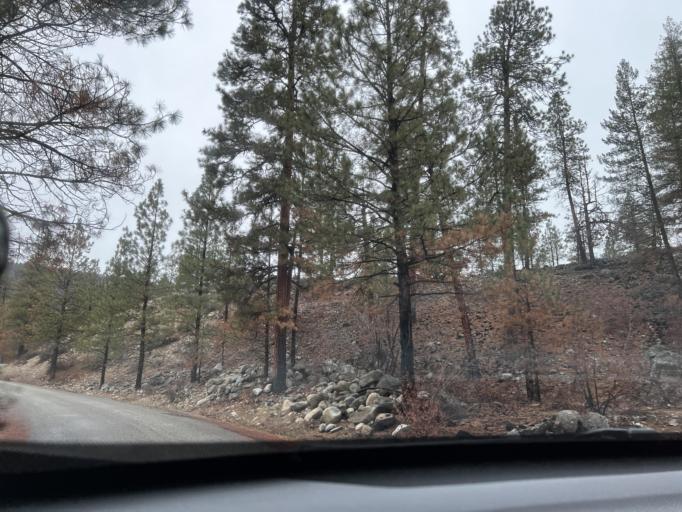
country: US
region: Washington
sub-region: Okanogan County
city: Brewster
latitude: 48.5797
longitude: -120.1656
